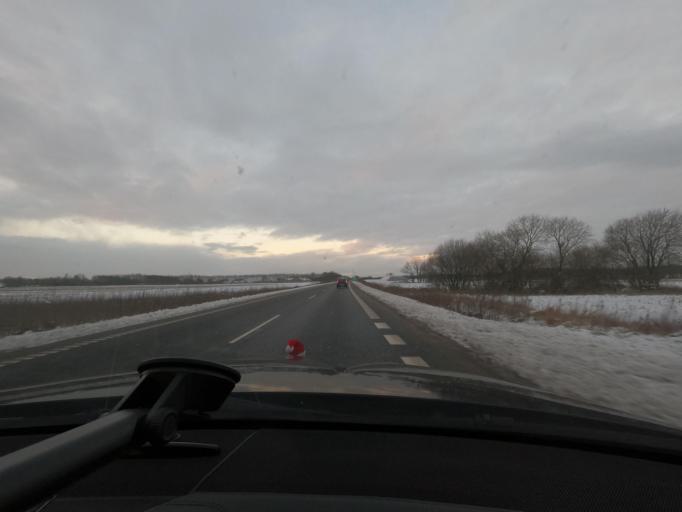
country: DK
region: South Denmark
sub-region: Aabenraa Kommune
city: Krusa
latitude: 54.8518
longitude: 9.4199
